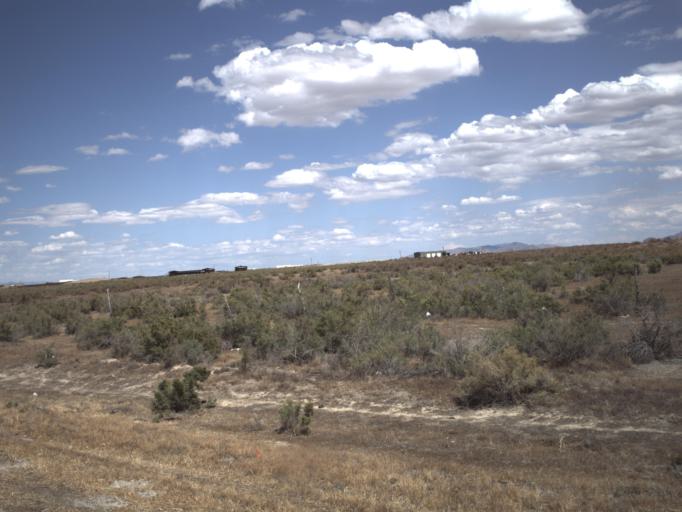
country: US
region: Utah
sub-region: Millard County
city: Delta
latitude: 39.3121
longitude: -112.4776
